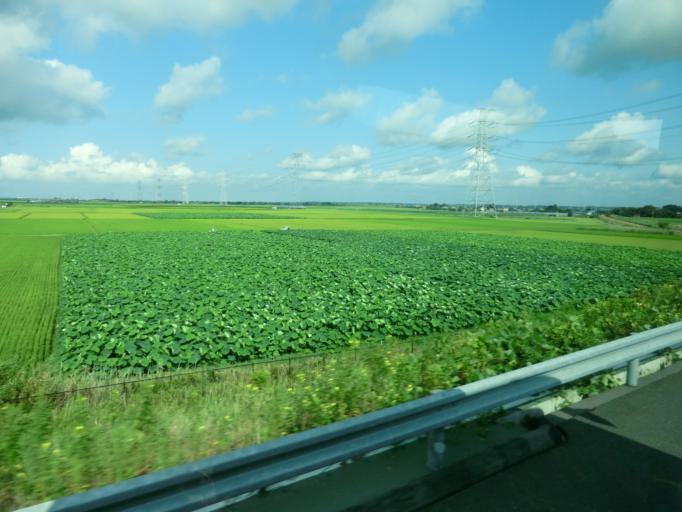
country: JP
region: Ibaraki
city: Inashiki
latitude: 35.8896
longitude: 140.3818
